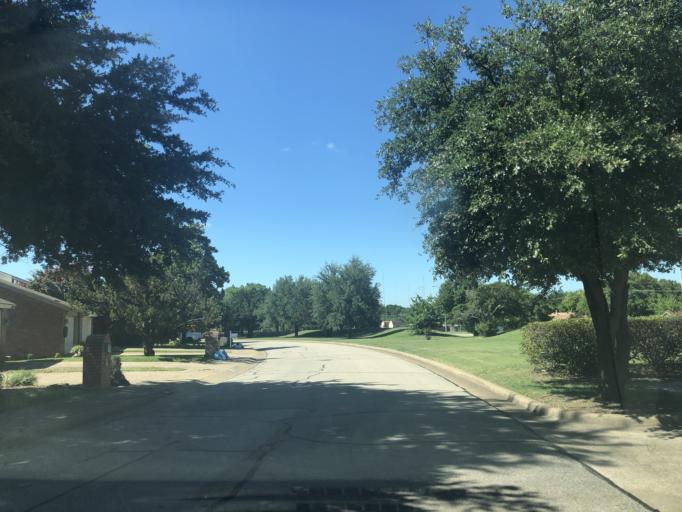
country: US
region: Texas
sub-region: Dallas County
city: Duncanville
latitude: 32.6458
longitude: -96.9422
